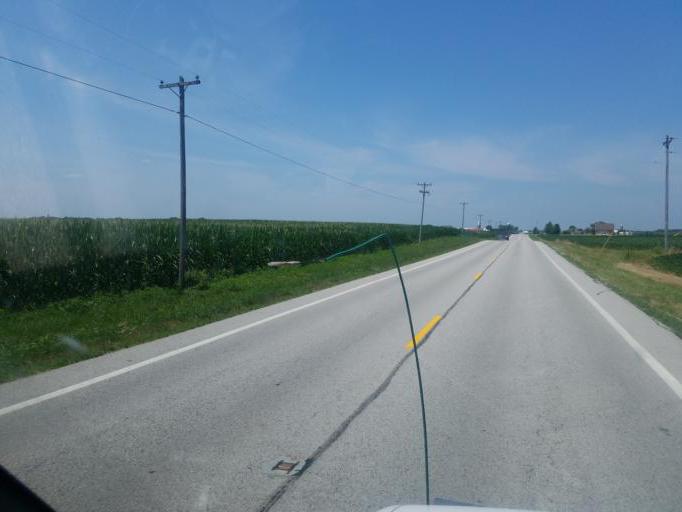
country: US
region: Ohio
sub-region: Auglaize County
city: New Bremen
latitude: 40.4455
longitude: -84.4340
